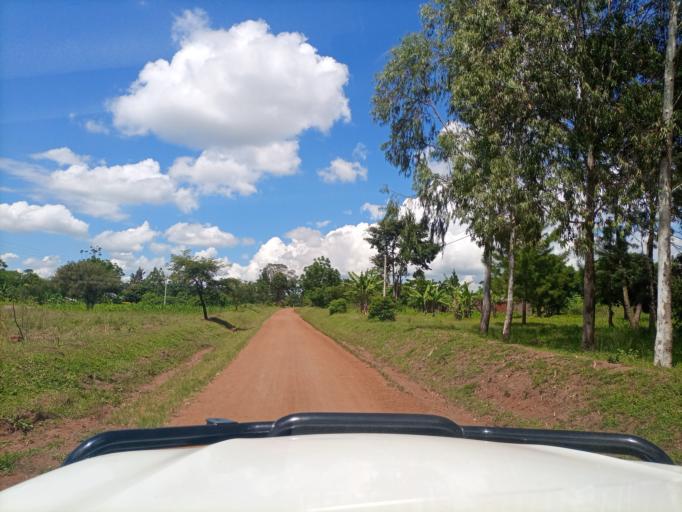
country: UG
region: Eastern Region
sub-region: Tororo District
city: Tororo
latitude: 0.7024
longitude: 34.0133
